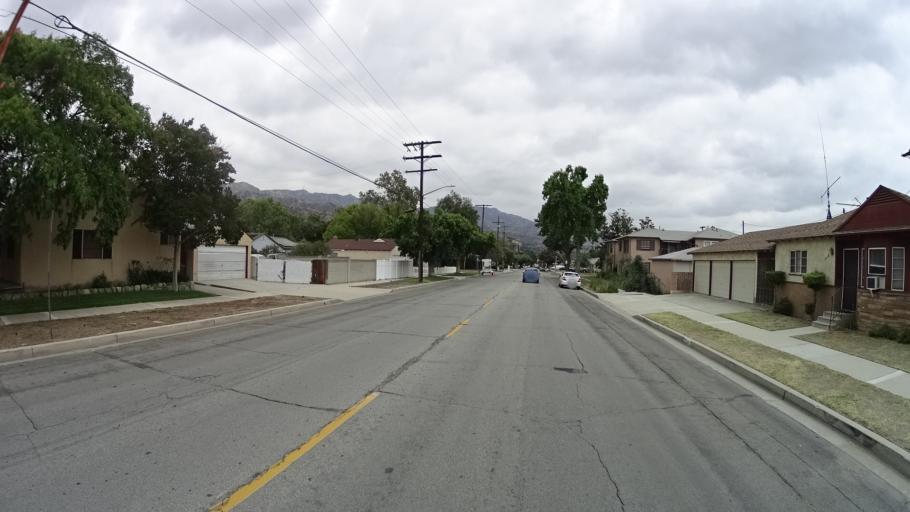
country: US
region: California
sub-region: Los Angeles County
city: Burbank
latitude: 34.1991
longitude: -118.3323
